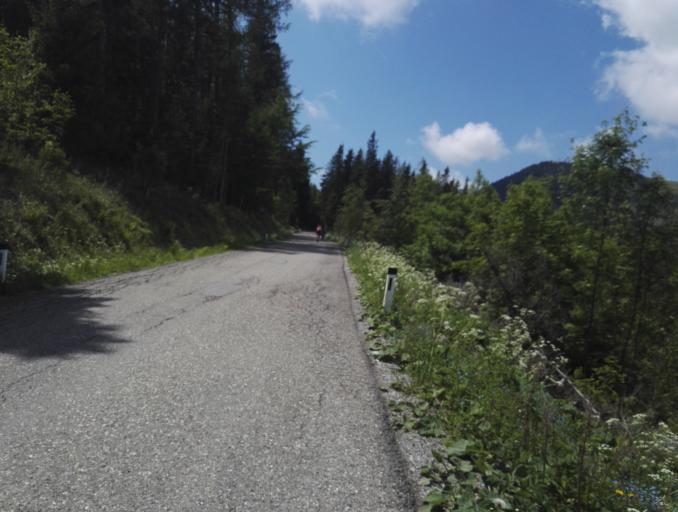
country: AT
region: Styria
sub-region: Politischer Bezirk Weiz
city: Stenzengreith
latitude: 47.2113
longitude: 15.4907
